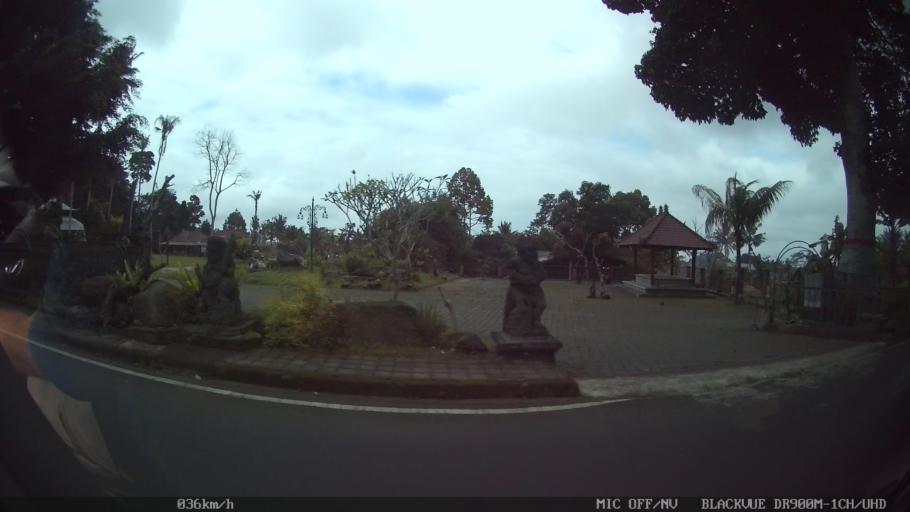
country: ID
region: Bali
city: Banjar Brahmanabukit
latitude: -8.4447
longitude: 115.3597
